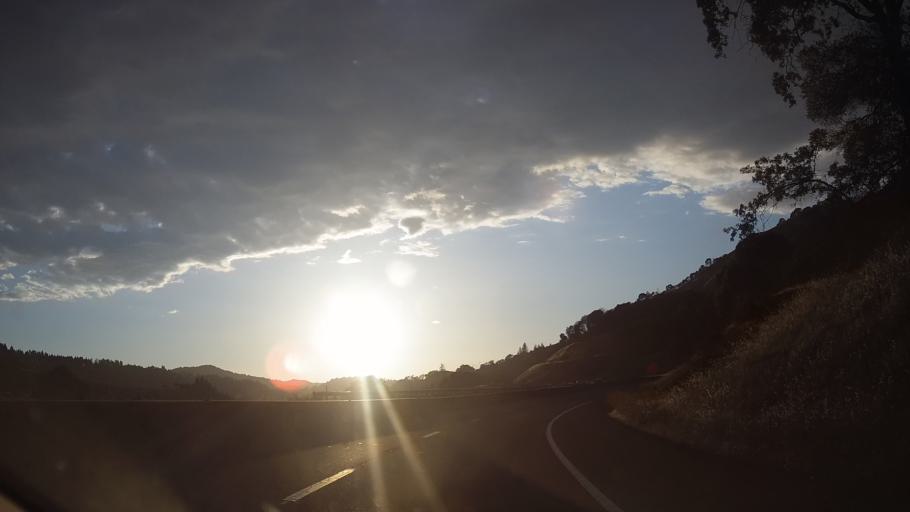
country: US
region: California
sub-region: Mendocino County
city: Redwood Valley
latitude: 39.2942
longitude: -123.2767
